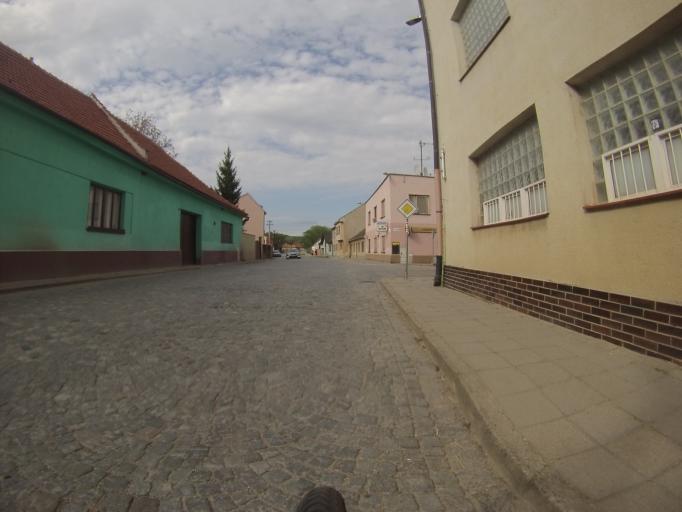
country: CZ
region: South Moravian
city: Veverska Bityska
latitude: 49.2765
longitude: 16.4373
